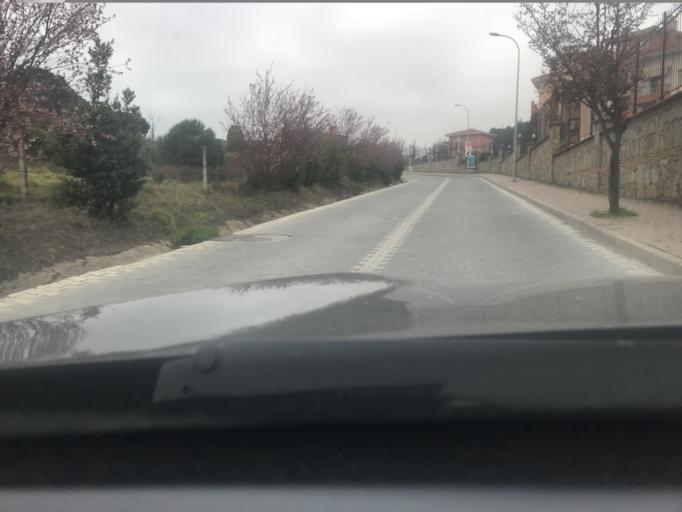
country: TR
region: Istanbul
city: Umraniye
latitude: 41.0380
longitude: 29.1572
